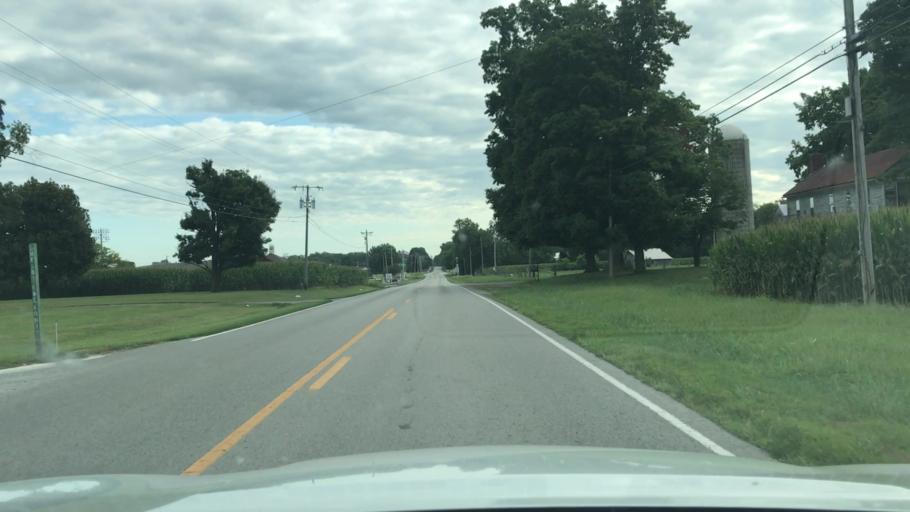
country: US
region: Kentucky
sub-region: Todd County
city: Elkton
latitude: 36.7934
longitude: -87.1625
